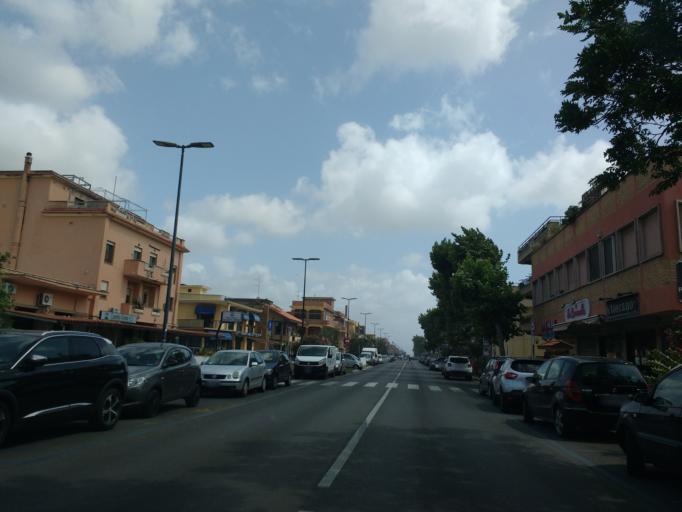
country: IT
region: Latium
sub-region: Citta metropolitana di Roma Capitale
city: Torvaianica
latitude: 41.6223
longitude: 12.4610
